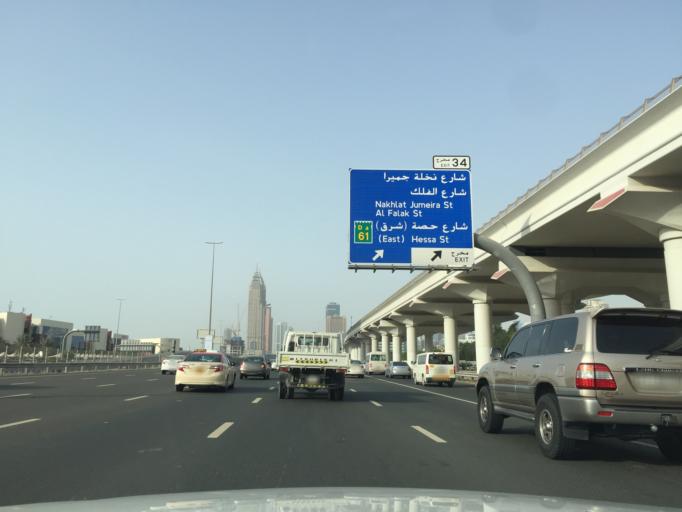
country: AE
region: Dubai
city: Dubai
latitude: 25.0878
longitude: 55.1566
